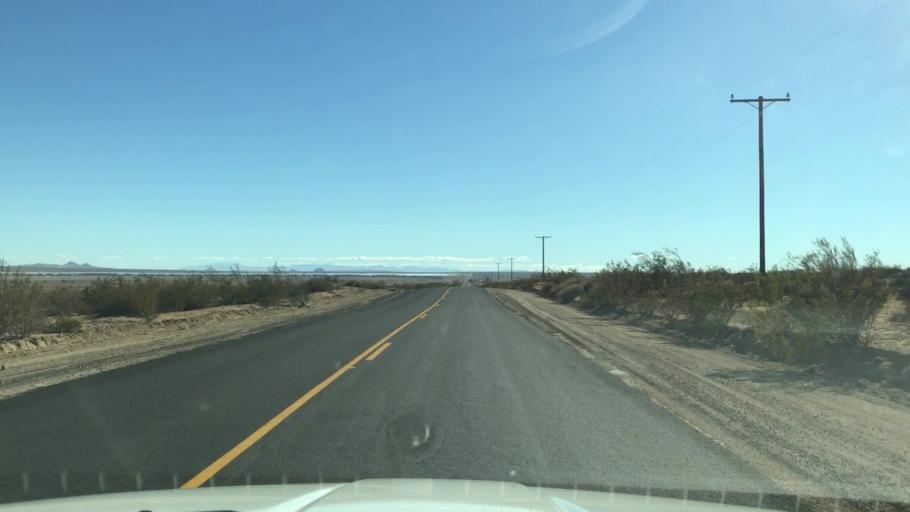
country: US
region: California
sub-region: Kern County
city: California City
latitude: 35.3092
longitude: -117.9860
